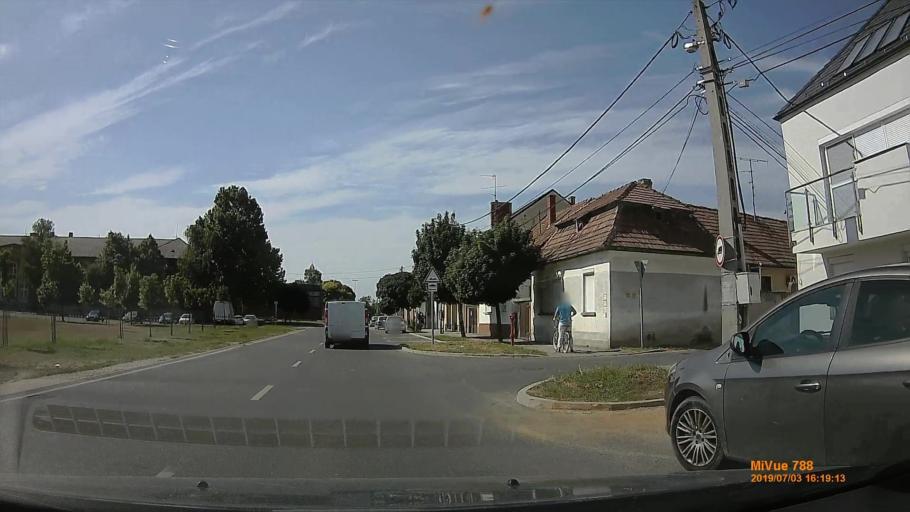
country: HU
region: Gyor-Moson-Sopron
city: Gyor
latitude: 47.6843
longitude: 17.6181
